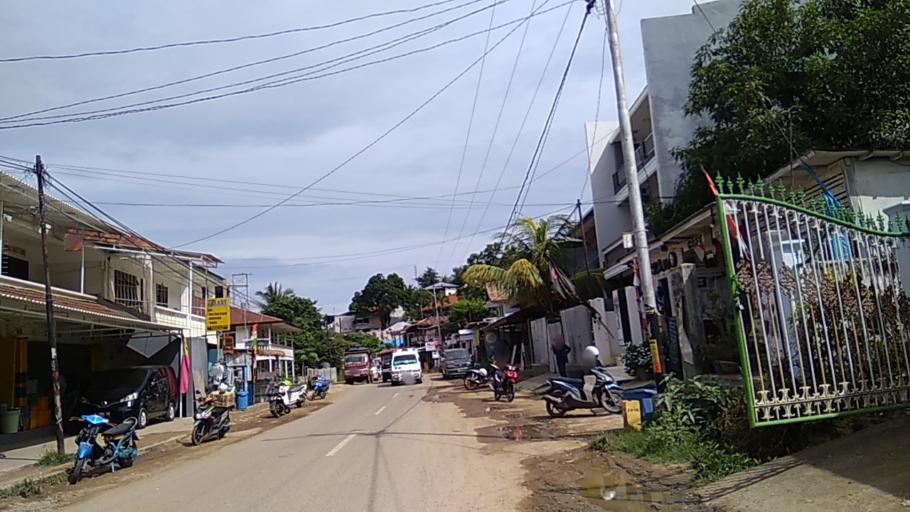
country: ID
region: East Nusa Tenggara
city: Cempa
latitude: -8.4944
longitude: 119.8785
